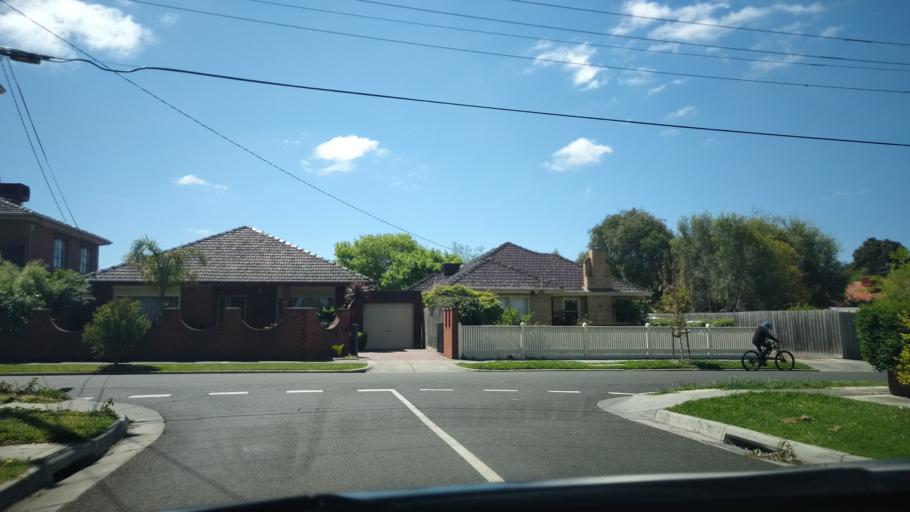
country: AU
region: Victoria
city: Hughesdale
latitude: -37.9049
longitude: 145.0788
